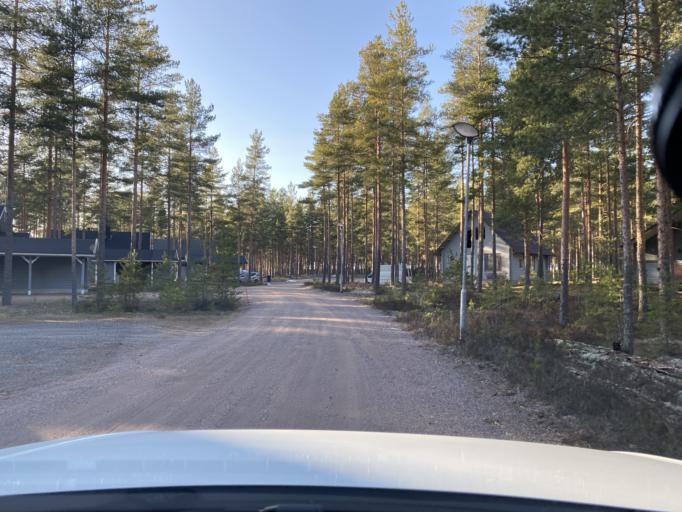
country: FI
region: Satakunta
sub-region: Pori
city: Vampula
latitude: 60.9702
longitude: 22.6702
